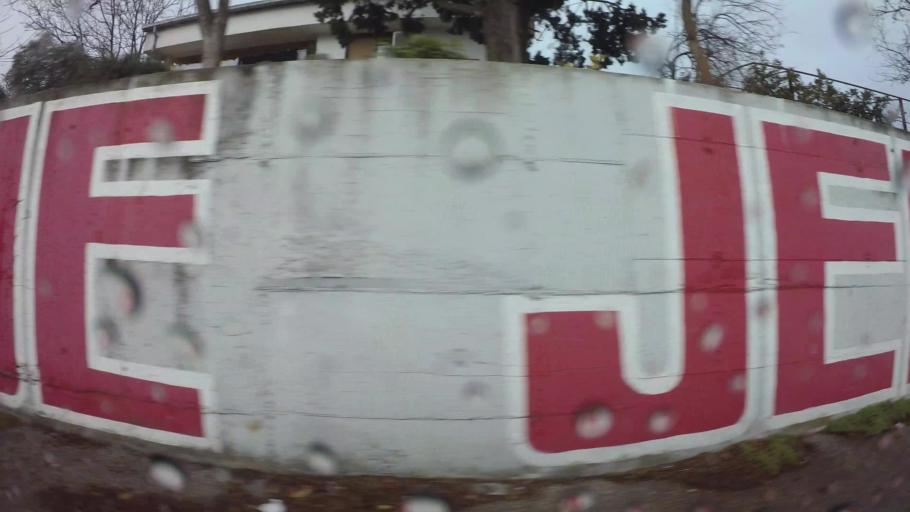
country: BA
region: Federation of Bosnia and Herzegovina
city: Cim
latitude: 43.3522
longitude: 17.7798
